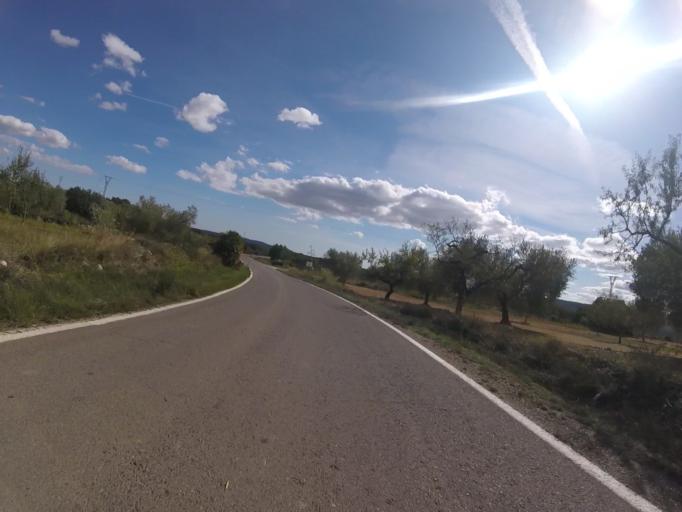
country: ES
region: Valencia
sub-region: Provincia de Castello
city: Albocasser
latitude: 40.3993
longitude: 0.0862
